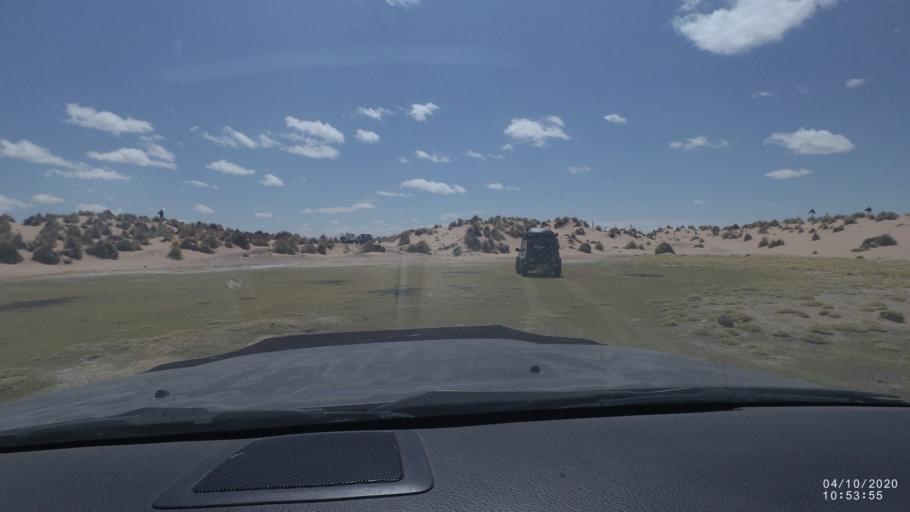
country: BO
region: Oruro
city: Poopo
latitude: -18.7012
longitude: -67.4678
